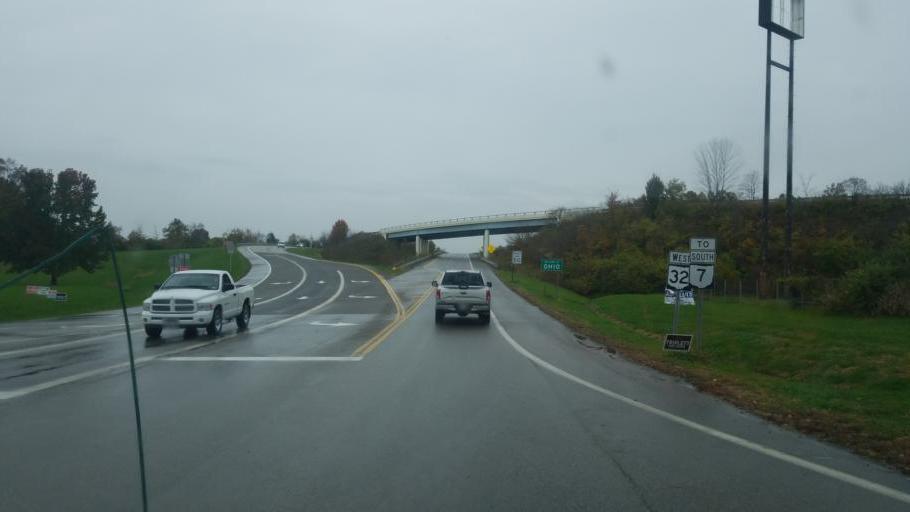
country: US
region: Ohio
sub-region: Washington County
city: Belpre
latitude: 39.2836
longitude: -81.5687
